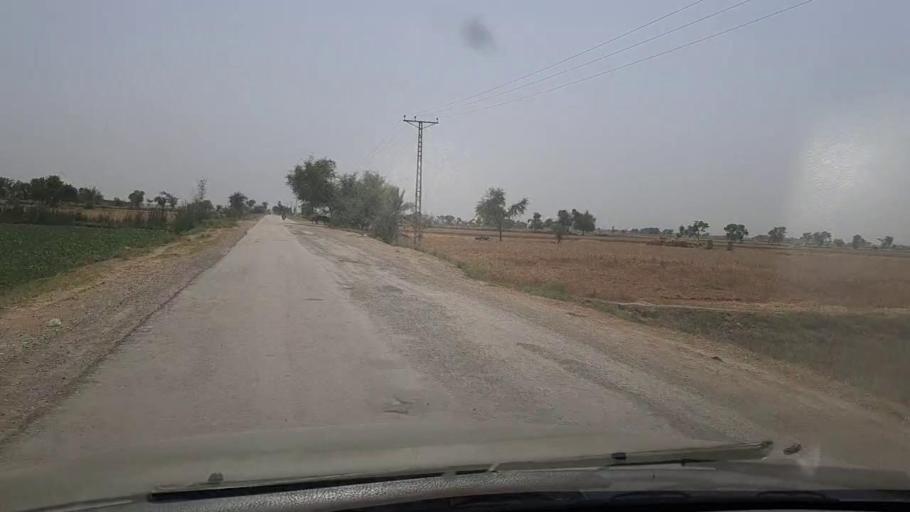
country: PK
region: Sindh
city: Miro Khan
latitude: 27.7139
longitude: 68.0661
